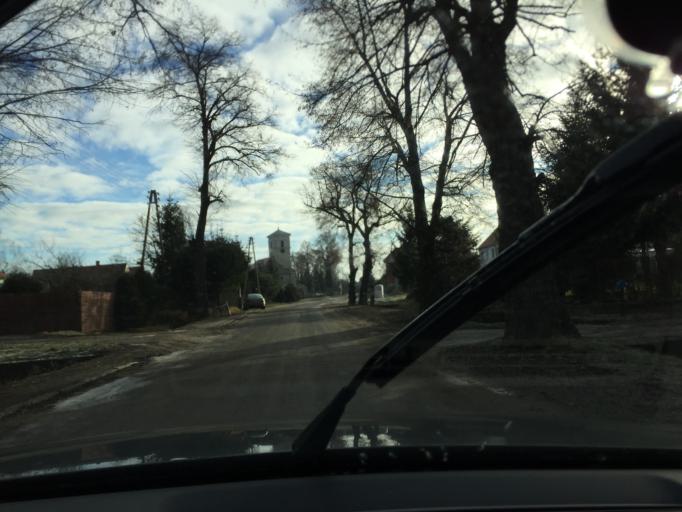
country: PL
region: Lower Silesian Voivodeship
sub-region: Powiat sredzki
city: Udanin
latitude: 51.0591
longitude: 16.4840
